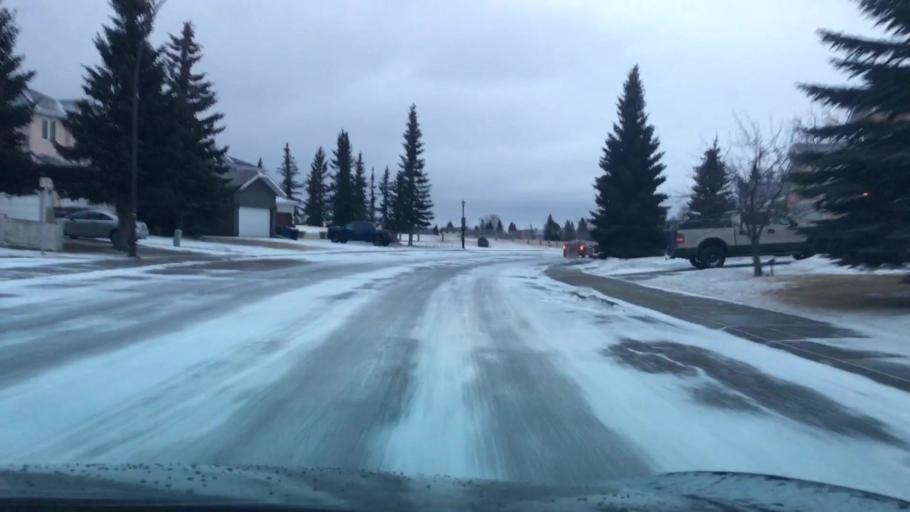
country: CA
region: Alberta
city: Calgary
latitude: 51.1330
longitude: -114.1664
